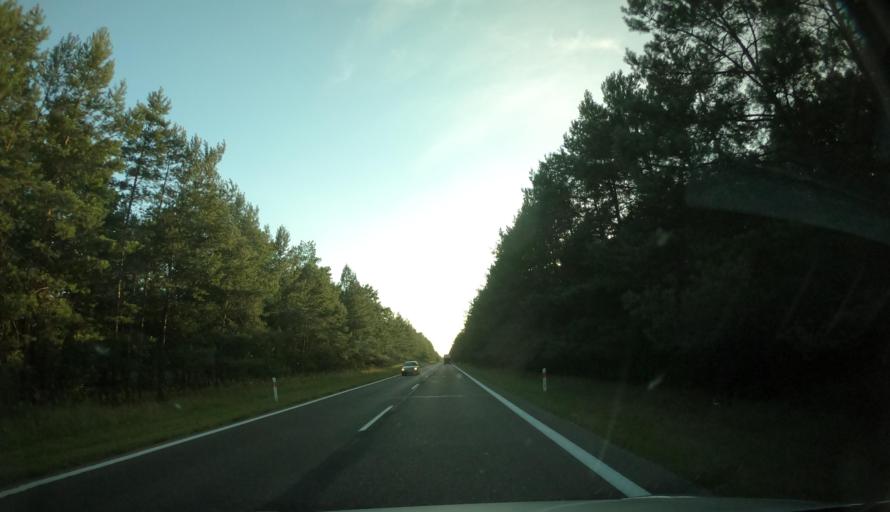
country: PL
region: Kujawsko-Pomorskie
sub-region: Powiat bydgoski
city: Koronowo
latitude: 53.3116
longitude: 18.0188
